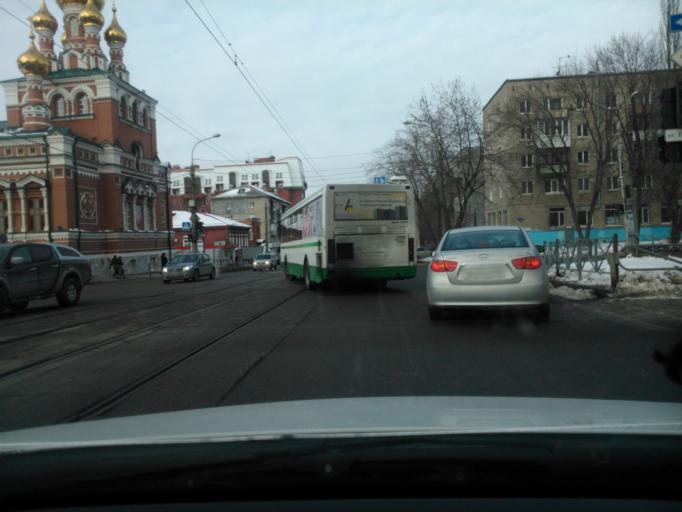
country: RU
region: Perm
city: Perm
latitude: 58.0053
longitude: 56.2218
